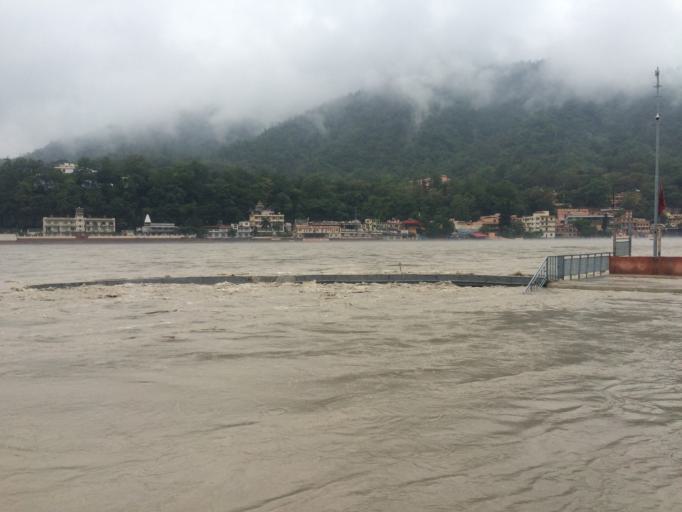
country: IN
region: Uttarakhand
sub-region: Dehradun
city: Rishikesh
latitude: 30.1194
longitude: 78.3117
